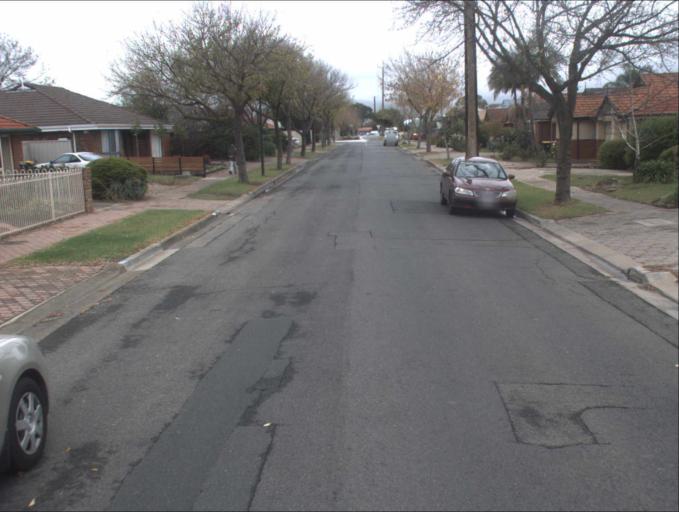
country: AU
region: South Australia
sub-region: Port Adelaide Enfield
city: Gilles Plains
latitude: -34.8589
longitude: 138.6402
